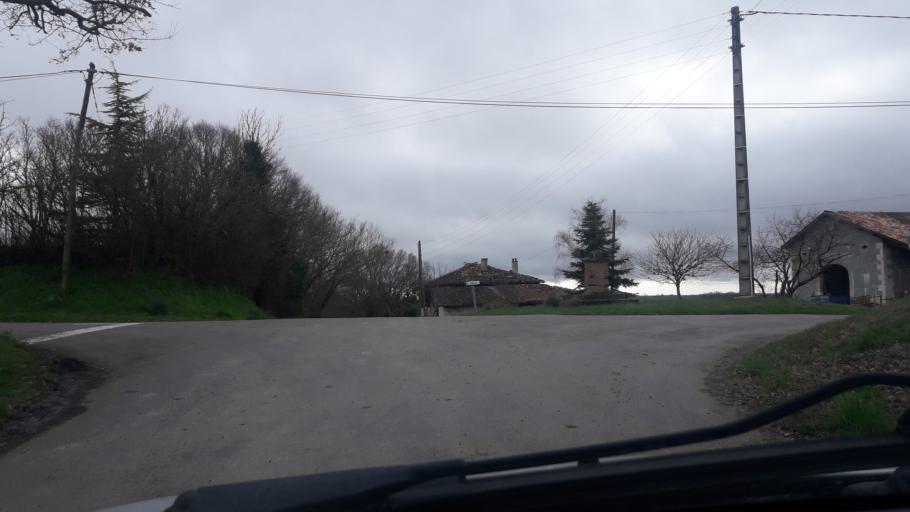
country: FR
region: Midi-Pyrenees
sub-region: Departement du Gers
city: Gimont
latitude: 43.6507
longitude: 0.9658
